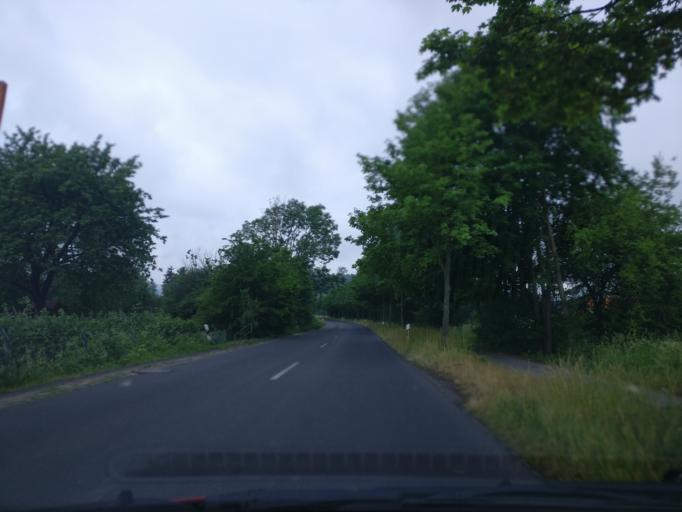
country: DE
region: Lower Saxony
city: Scheden
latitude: 51.3926
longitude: 9.7562
